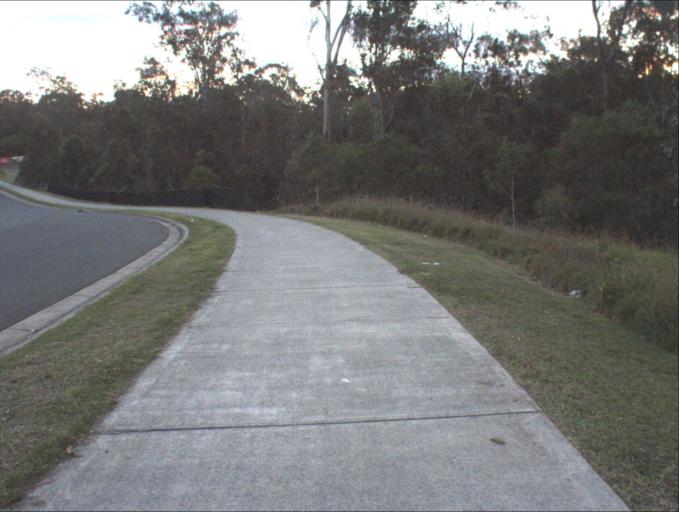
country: AU
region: Queensland
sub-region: Logan
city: North Maclean
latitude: -27.8037
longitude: 152.9519
